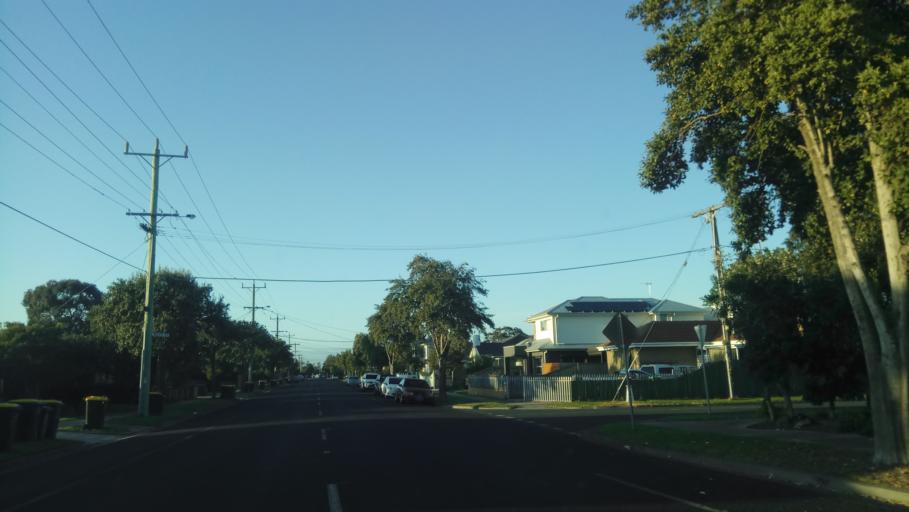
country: AU
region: Victoria
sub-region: Hobsons Bay
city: Altona
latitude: -37.8668
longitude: 144.8180
